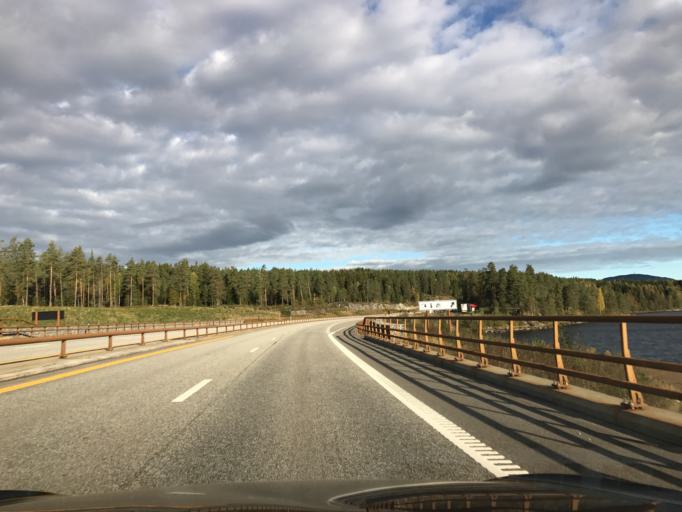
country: NO
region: Akershus
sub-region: Eidsvoll
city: Raholt
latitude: 60.2861
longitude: 11.1352
